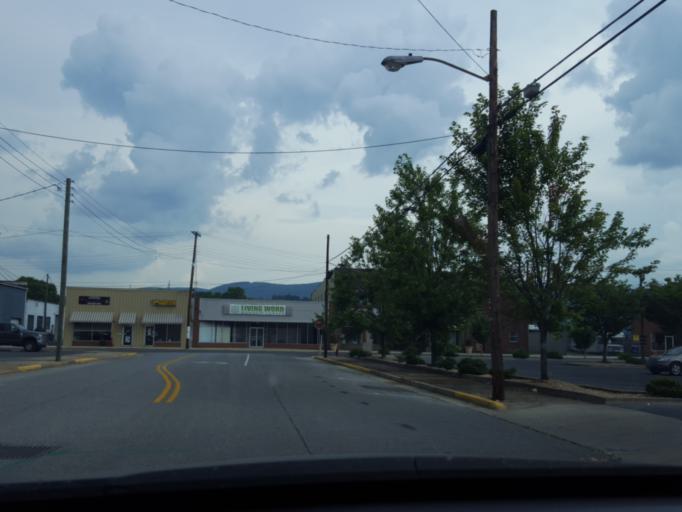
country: US
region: Virginia
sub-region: City of Waynesboro
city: Waynesboro
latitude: 38.0677
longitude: -78.8880
